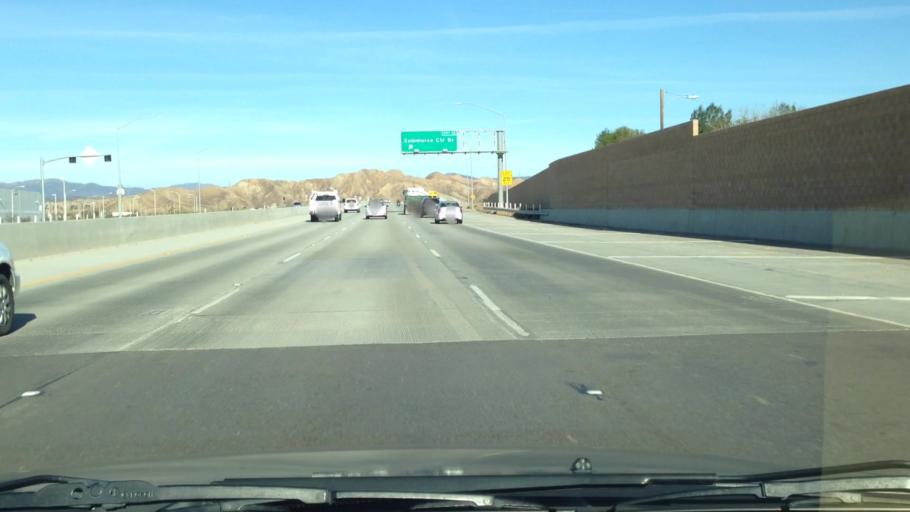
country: US
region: California
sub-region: Los Angeles County
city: Valencia
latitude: 34.4310
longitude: -118.6232
